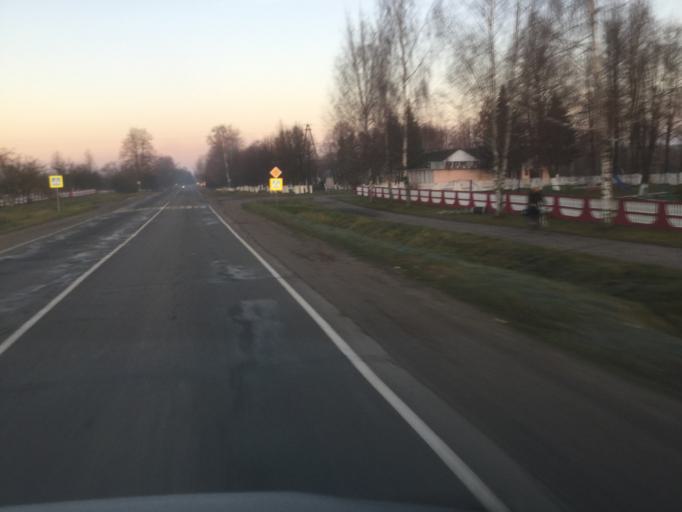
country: BY
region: Vitebsk
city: Vyerkhnyadzvinsk
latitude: 55.7093
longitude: 28.0897
